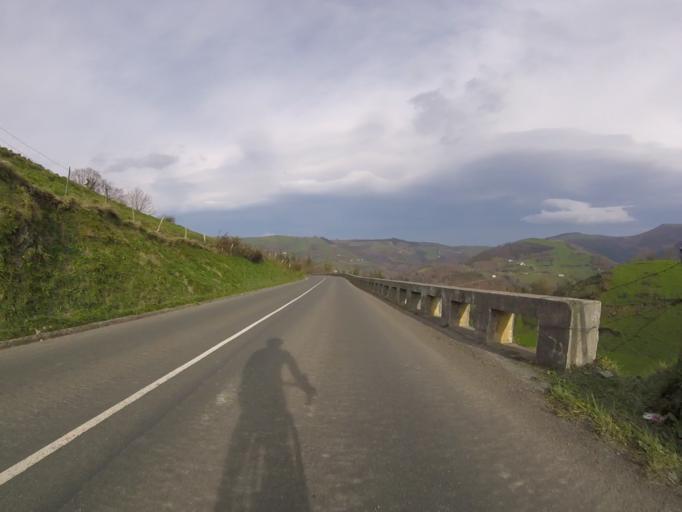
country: ES
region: Basque Country
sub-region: Provincia de Guipuzcoa
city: Beizama
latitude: 43.1670
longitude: -2.2218
